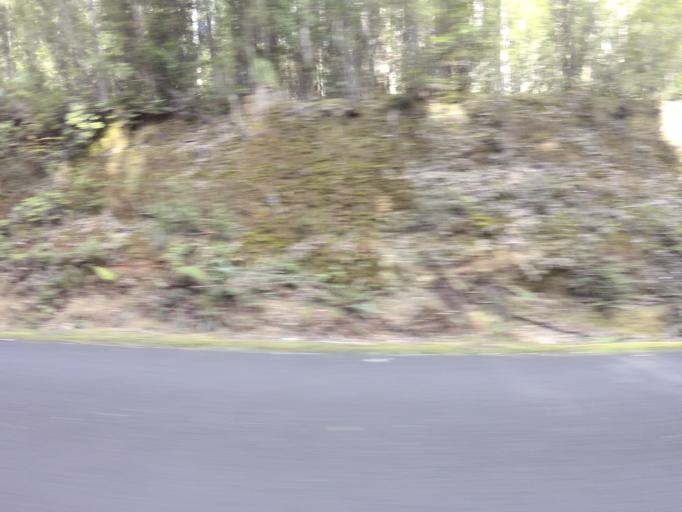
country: AU
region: Tasmania
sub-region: Huon Valley
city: Geeveston
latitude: -42.8247
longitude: 146.3153
